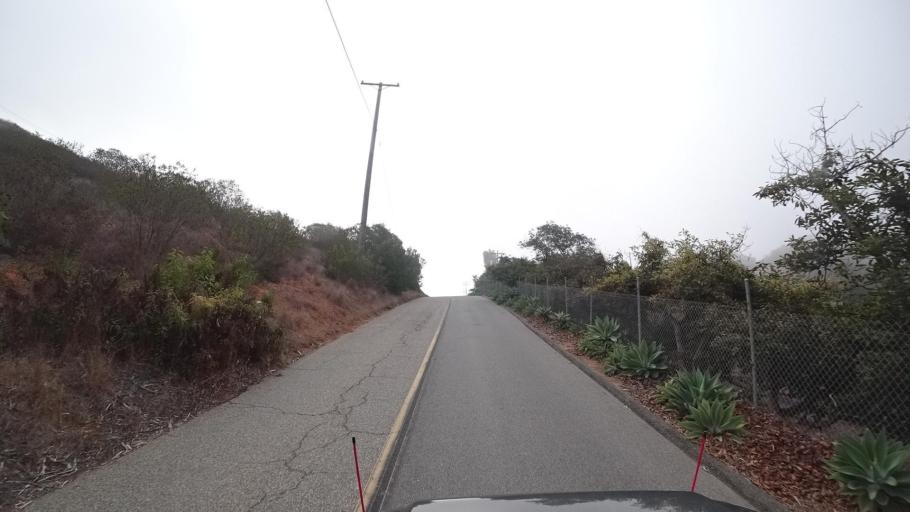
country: US
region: California
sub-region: San Diego County
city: Rainbow
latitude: 33.3475
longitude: -117.1765
